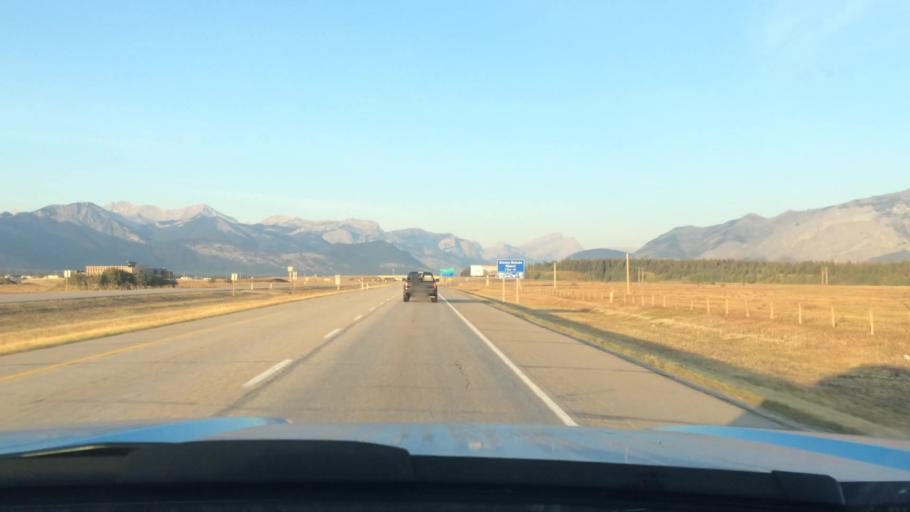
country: CA
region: Alberta
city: Canmore
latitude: 51.1093
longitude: -115.0073
